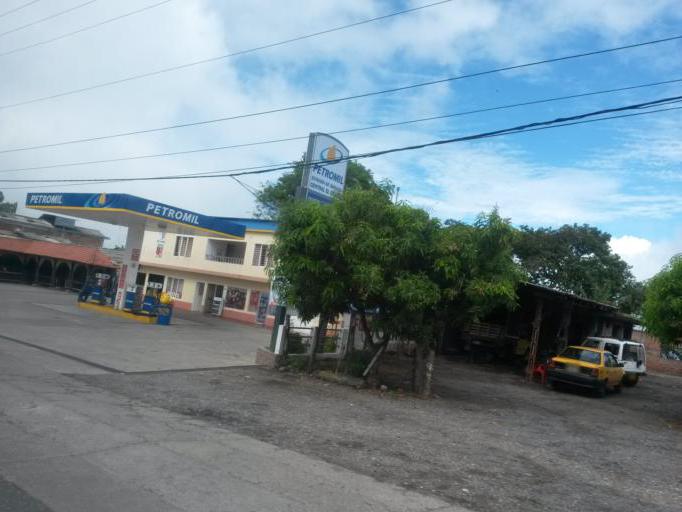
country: CO
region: Cauca
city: El Bordo
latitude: 2.1208
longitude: -76.9821
